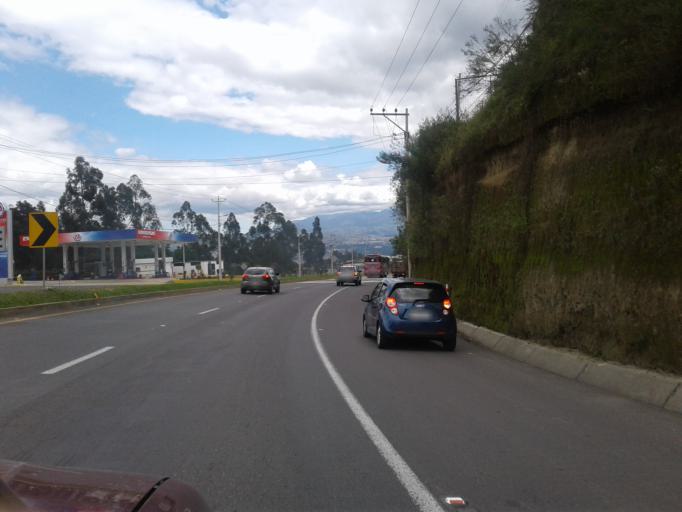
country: EC
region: Pichincha
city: Sangolqui
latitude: -0.3269
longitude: -78.3946
